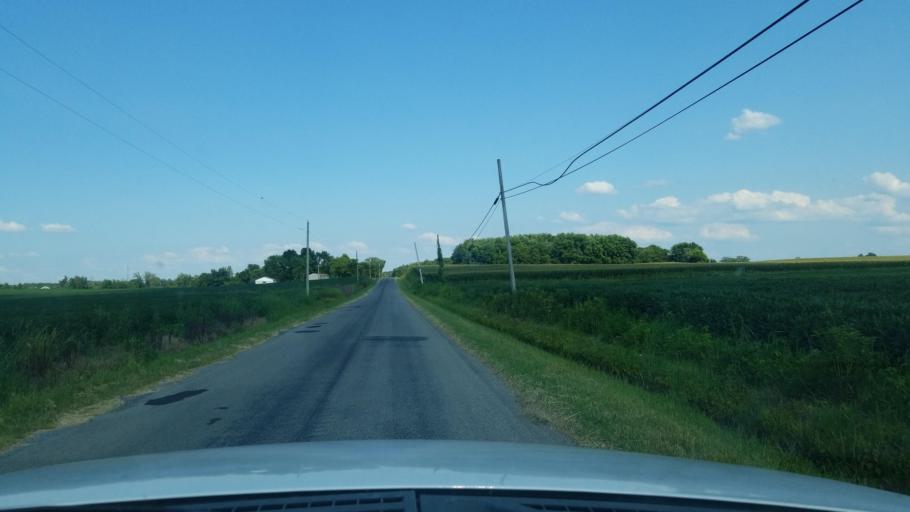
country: US
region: Illinois
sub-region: Saline County
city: Eldorado
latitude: 37.8048
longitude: -88.4748
